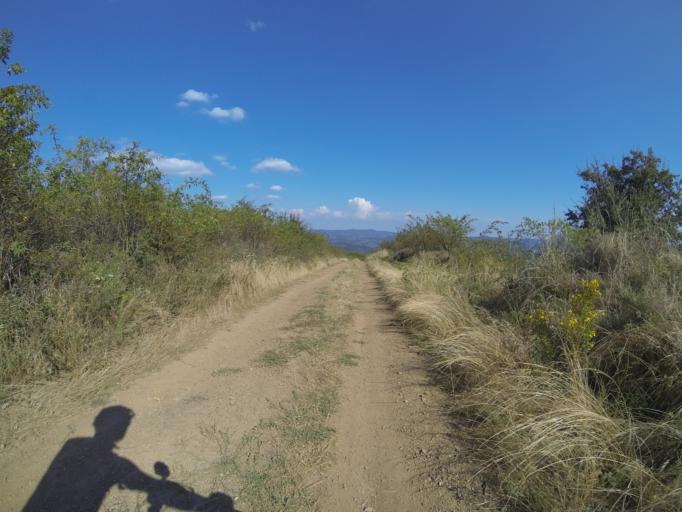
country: RO
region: Mehedinti
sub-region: Comuna Svinita
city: Svinita
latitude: 44.5626
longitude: 22.1532
